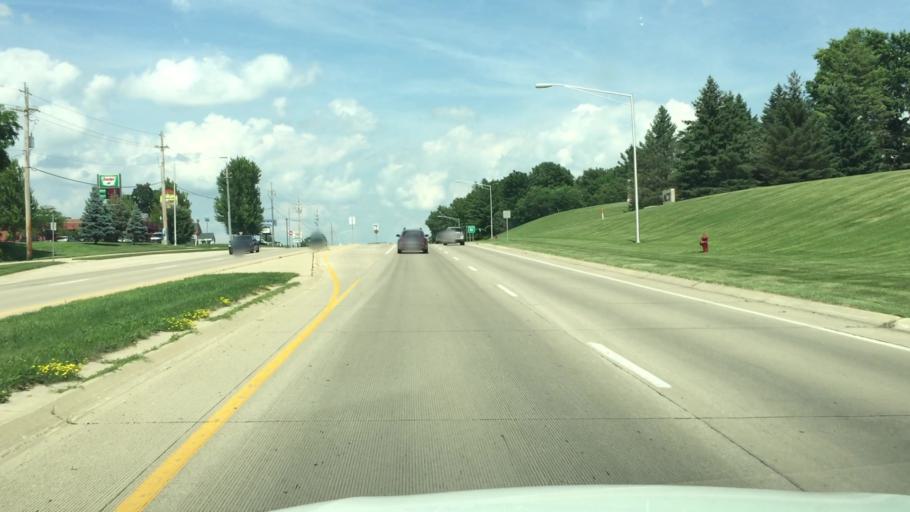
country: US
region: Iowa
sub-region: Johnson County
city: Iowa City
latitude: 41.6827
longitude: -91.5051
